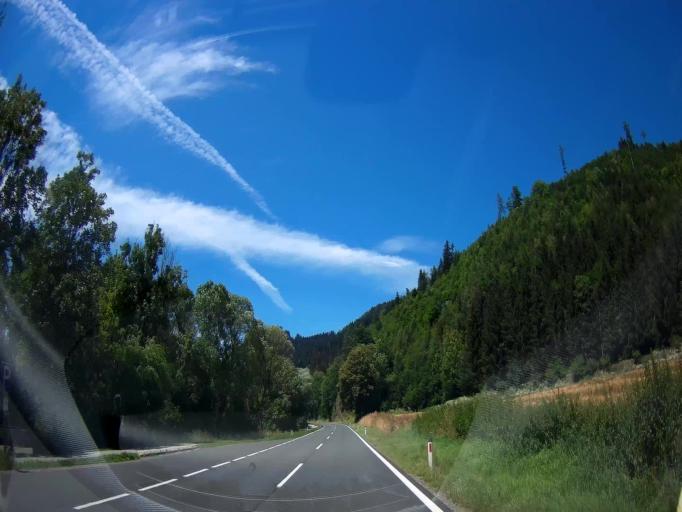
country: AT
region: Carinthia
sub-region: Politischer Bezirk Sankt Veit an der Glan
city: Micheldorf
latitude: 46.9032
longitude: 14.4078
